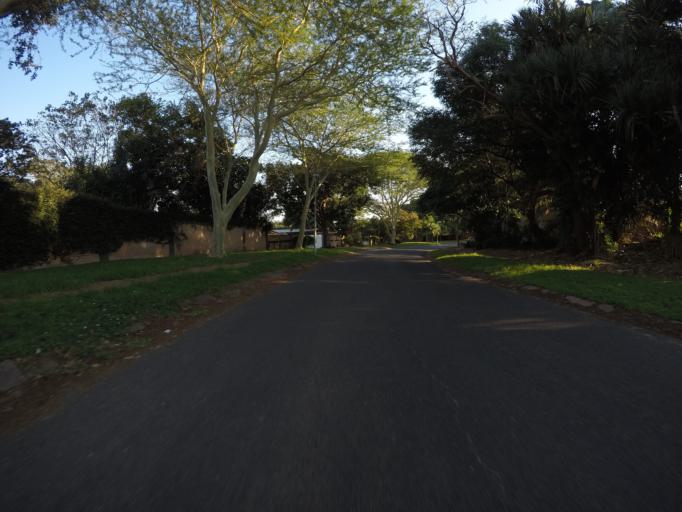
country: ZA
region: KwaZulu-Natal
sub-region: uThungulu District Municipality
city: Richards Bay
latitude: -28.7746
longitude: 32.1041
